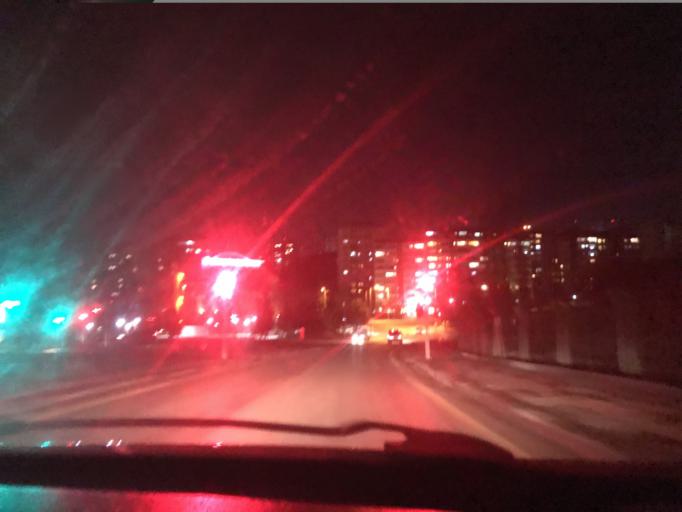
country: TR
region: Ankara
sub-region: Goelbasi
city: Golbasi
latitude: 39.8486
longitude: 32.8111
